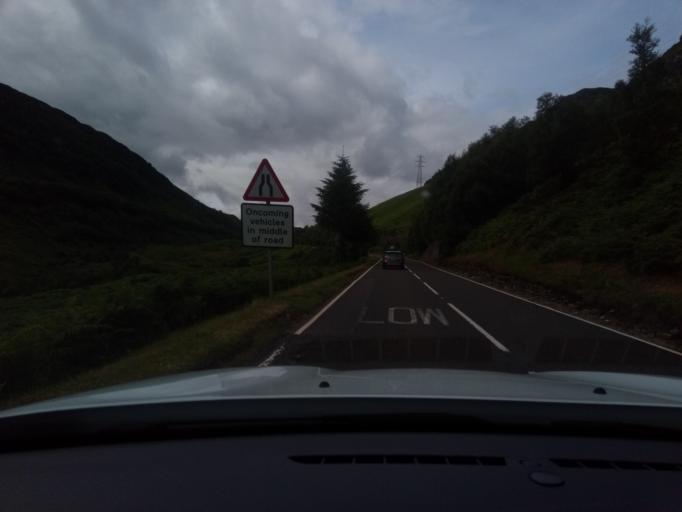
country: GB
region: Scotland
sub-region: Stirling
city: Callander
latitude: 56.4093
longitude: -4.3109
